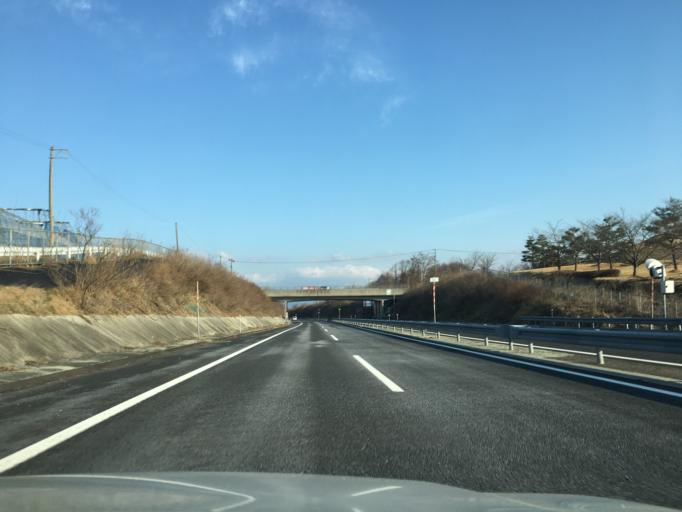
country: JP
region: Yamagata
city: Sagae
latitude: 38.3651
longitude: 140.2661
